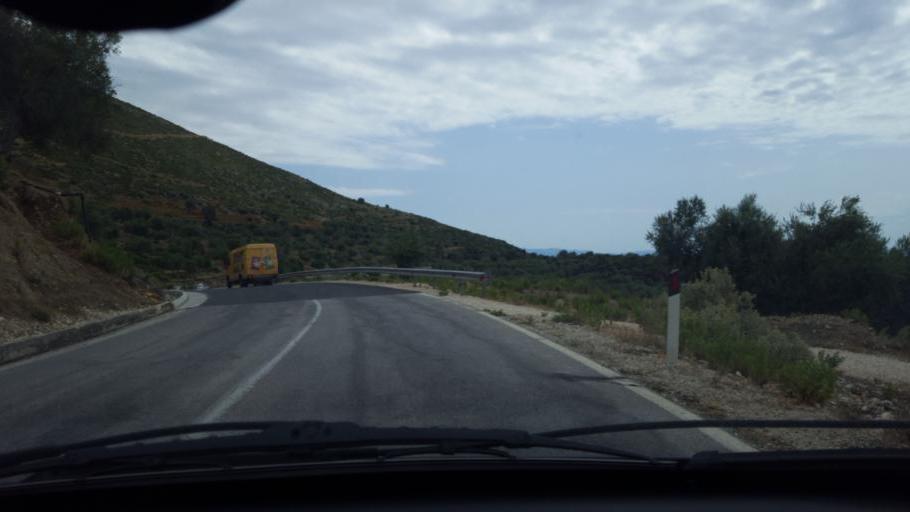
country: AL
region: Vlore
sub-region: Rrethi i Sarandes
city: Lukove
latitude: 40.0328
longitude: 19.8869
